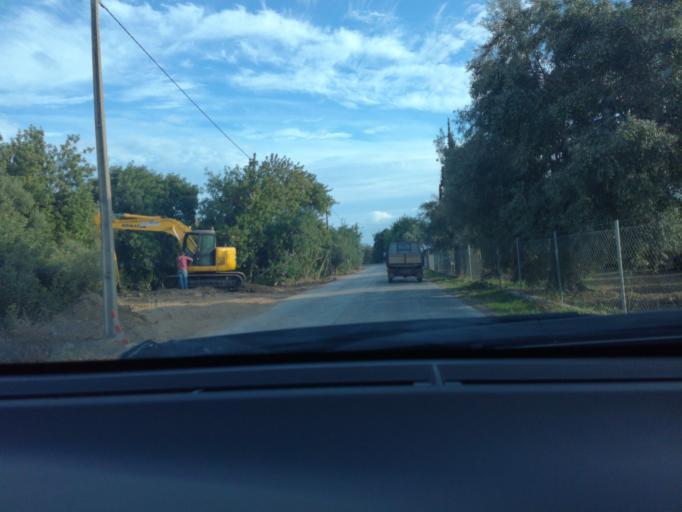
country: PT
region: Faro
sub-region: Olhao
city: Moncarapacho
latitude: 37.0774
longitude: -7.7765
